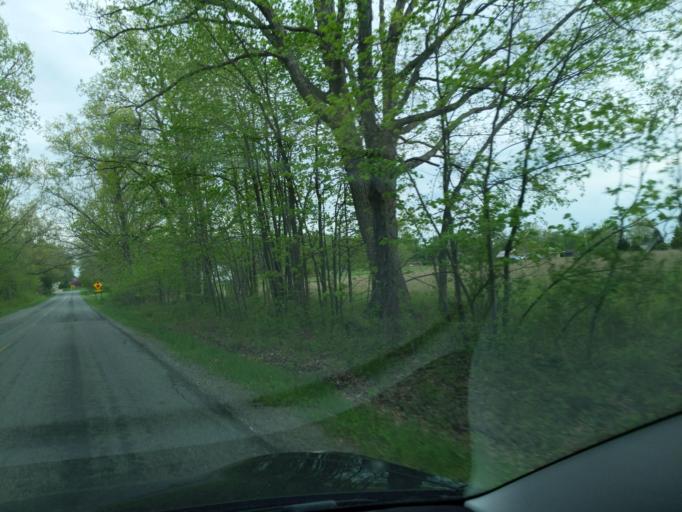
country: US
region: Michigan
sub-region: Ingham County
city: Stockbridge
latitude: 42.4271
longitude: -84.2583
